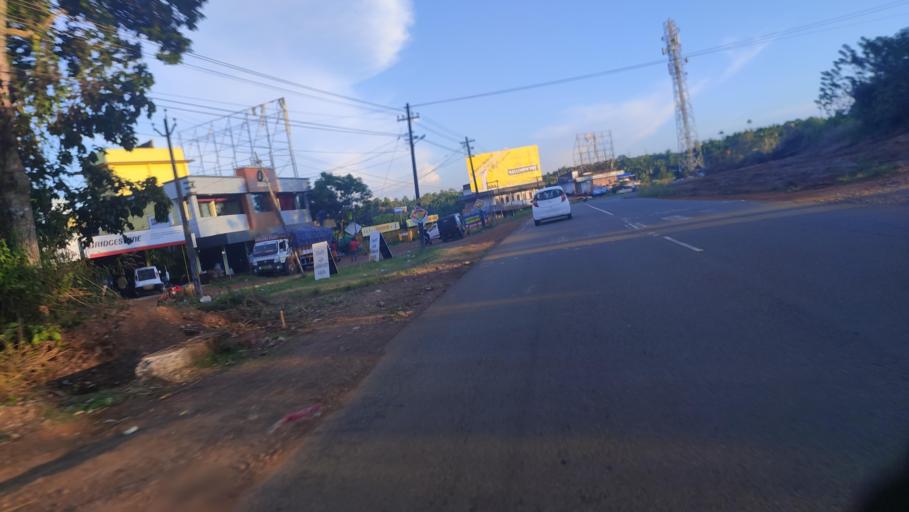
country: IN
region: Kerala
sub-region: Kasaragod District
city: Kannangad
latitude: 12.4076
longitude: 75.0959
